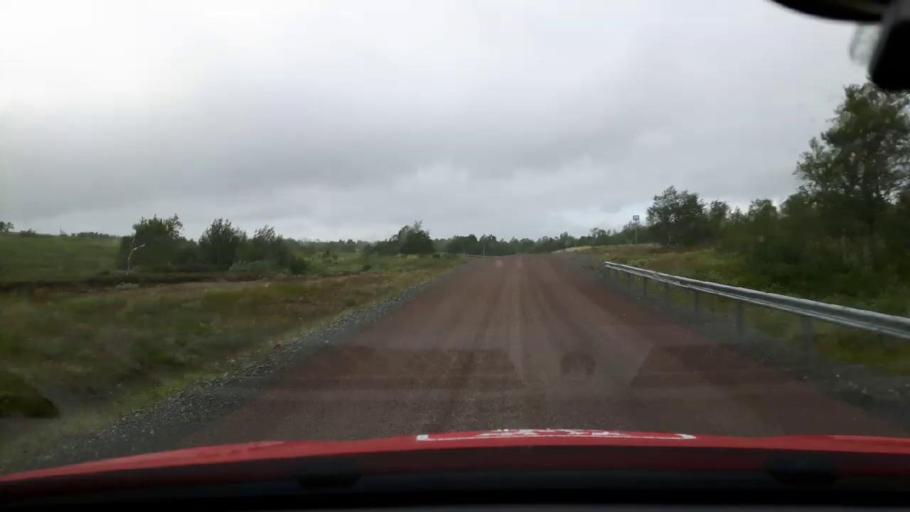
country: NO
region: Nord-Trondelag
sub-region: Meraker
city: Meraker
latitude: 63.2084
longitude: 12.4033
